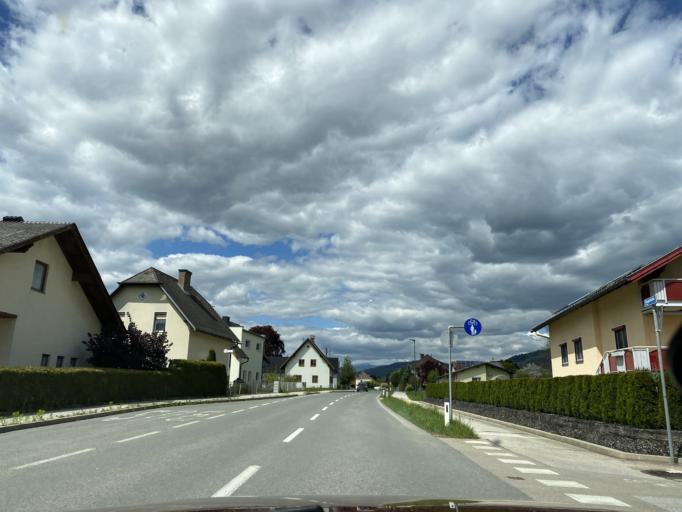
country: AT
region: Carinthia
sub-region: Politischer Bezirk Wolfsberg
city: Wolfsberg
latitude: 46.7997
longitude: 14.8512
